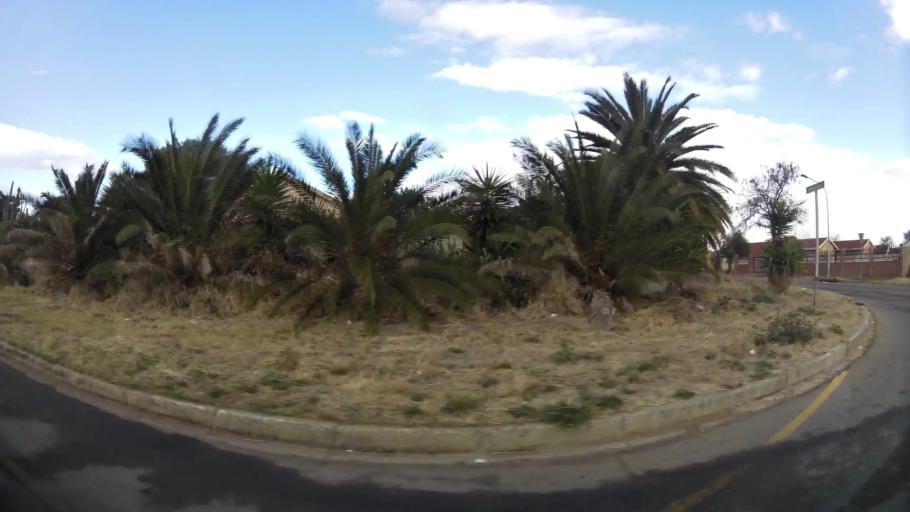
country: ZA
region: Orange Free State
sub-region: Lejweleputswa District Municipality
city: Welkom
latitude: -28.0008
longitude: 26.7388
